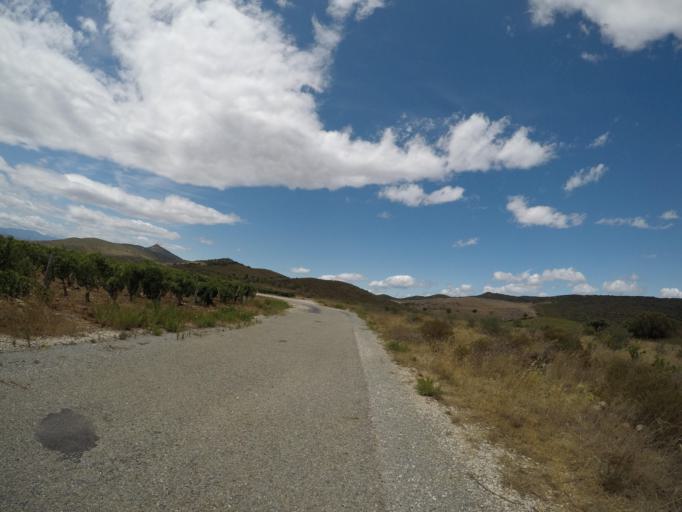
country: FR
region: Languedoc-Roussillon
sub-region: Departement des Pyrenees-Orientales
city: Corneilla-la-Riviere
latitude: 42.7250
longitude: 2.7482
